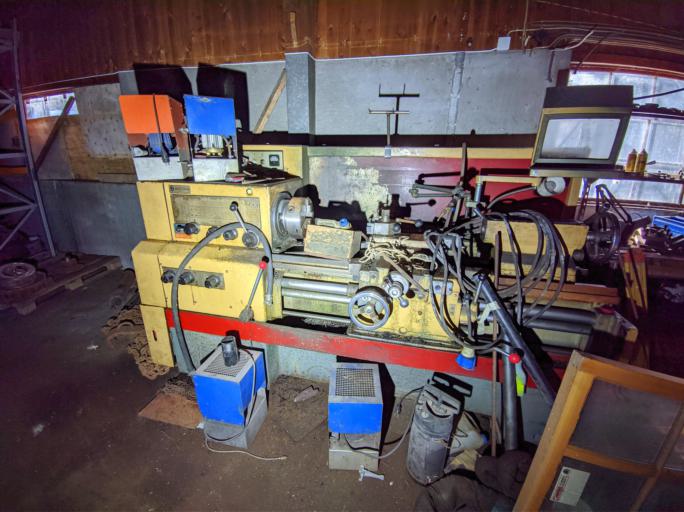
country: NO
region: Akershus
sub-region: Nannestad
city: Teigebyen
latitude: 60.1947
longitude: 10.9662
